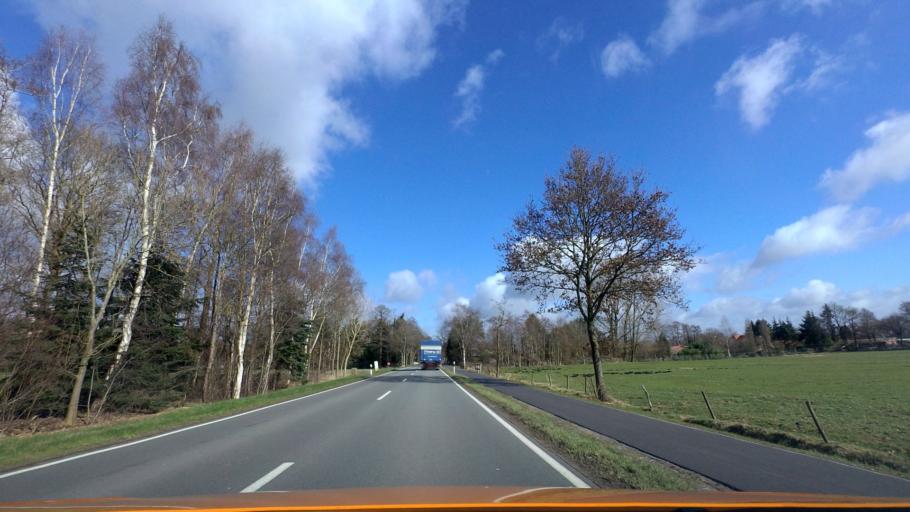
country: DE
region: Lower Saxony
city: Edewecht
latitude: 53.1072
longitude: 7.9533
